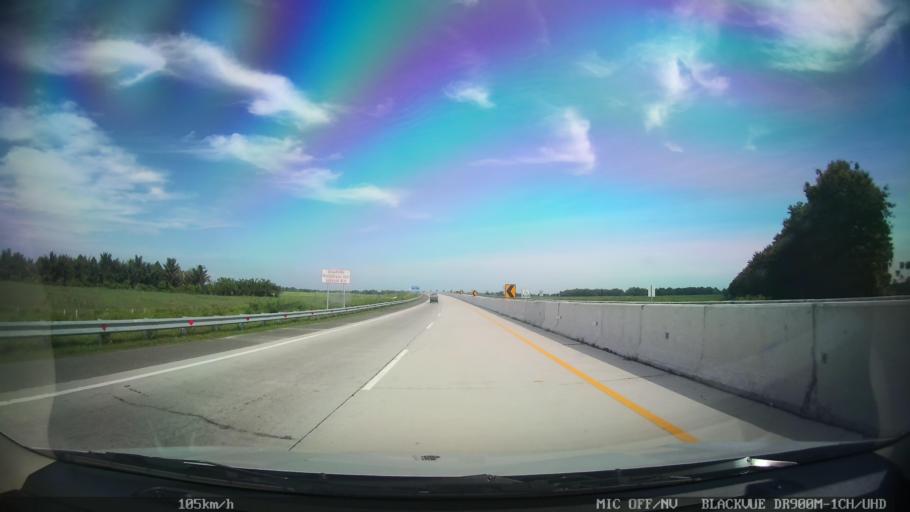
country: ID
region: North Sumatra
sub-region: Kabupaten Langkat
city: Stabat
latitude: 3.7044
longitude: 98.5382
